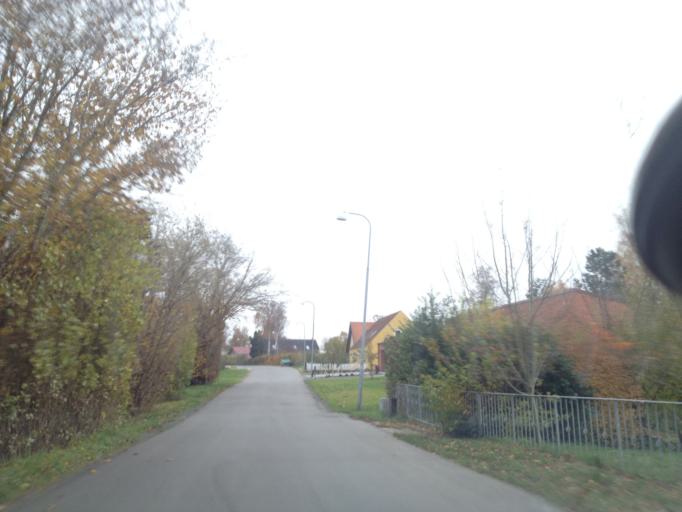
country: DK
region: South Denmark
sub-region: Nordfyns Kommune
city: Sonderso
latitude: 55.4231
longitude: 10.2485
